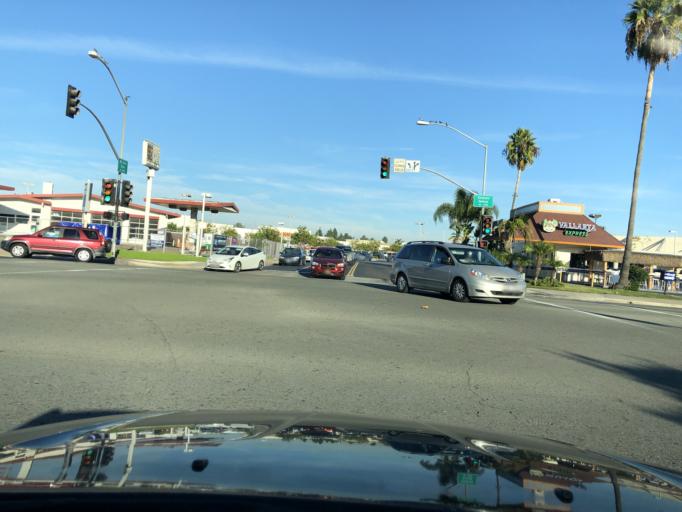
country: US
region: California
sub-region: San Diego County
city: La Jolla
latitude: 32.8213
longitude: -117.1831
